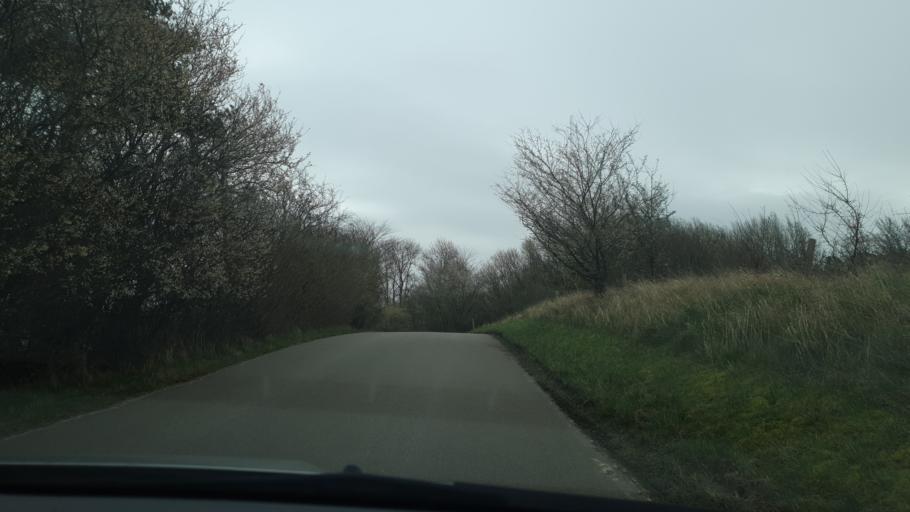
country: DK
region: Zealand
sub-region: Odsherred Kommune
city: Asnaes
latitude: 55.8356
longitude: 11.4269
